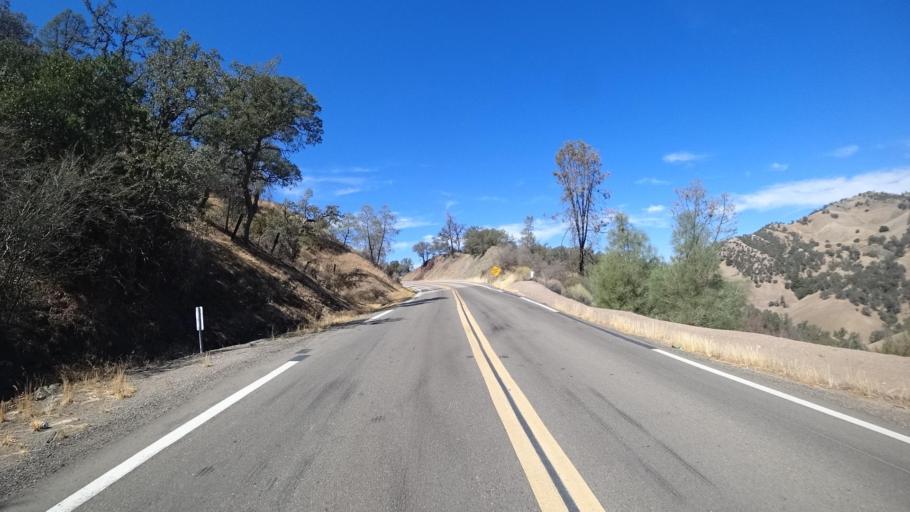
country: US
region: California
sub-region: Monterey County
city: King City
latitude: 36.1964
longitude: -120.7451
